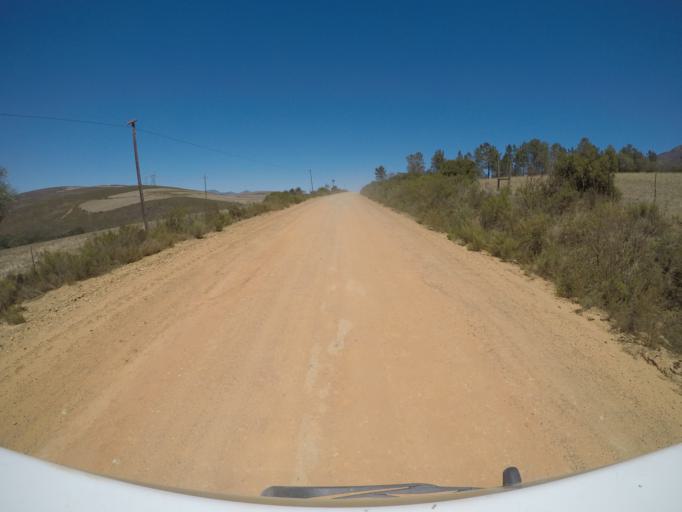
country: ZA
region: Western Cape
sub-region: Overberg District Municipality
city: Caledon
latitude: -34.1960
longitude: 19.2226
